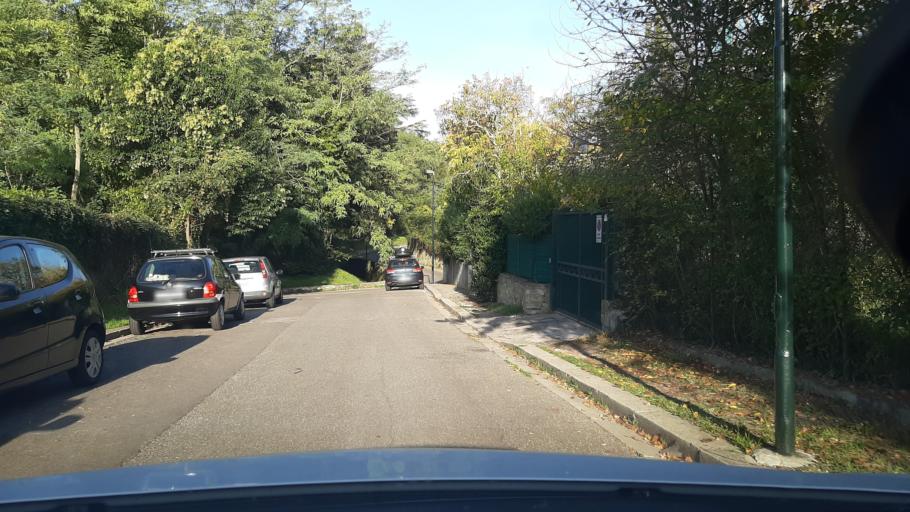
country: IT
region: Tuscany
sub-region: Province of Florence
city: Fiesole
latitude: 43.7895
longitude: 11.2943
